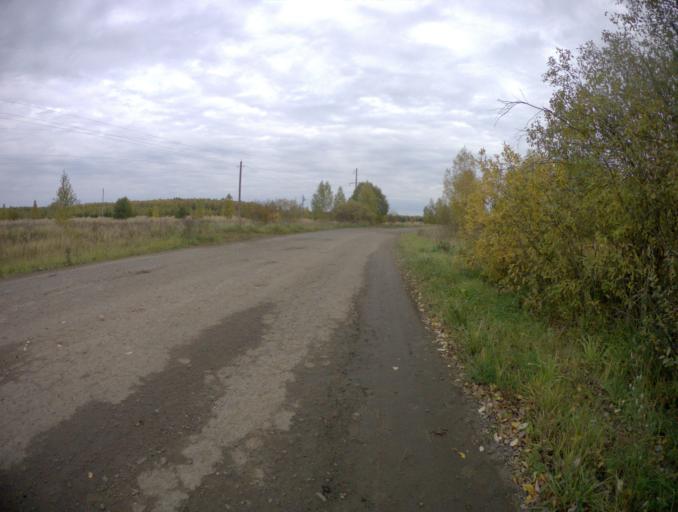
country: RU
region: Vladimir
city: Mstera
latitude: 56.3756
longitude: 41.8324
